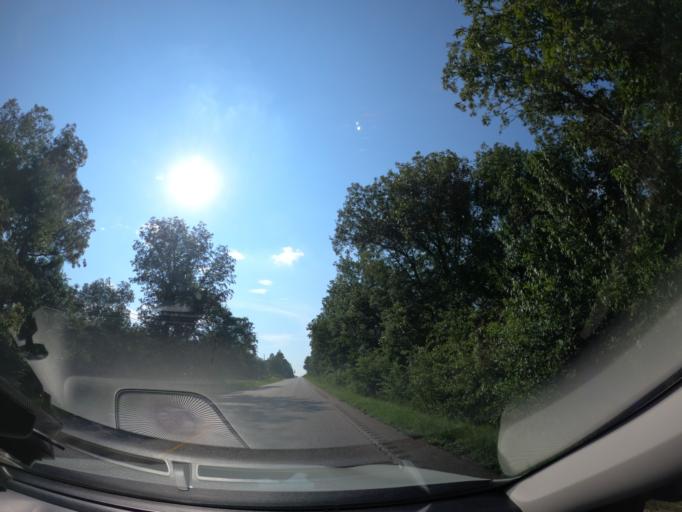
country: US
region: South Carolina
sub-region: Aiken County
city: Jackson
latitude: 33.4090
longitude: -81.7929
